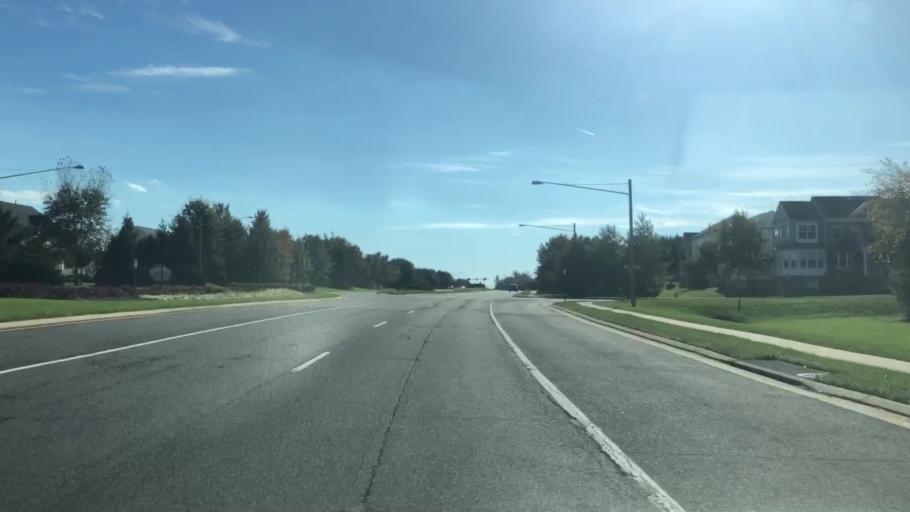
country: US
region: Virginia
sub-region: Prince William County
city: Linton Hall
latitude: 38.7448
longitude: -77.5758
